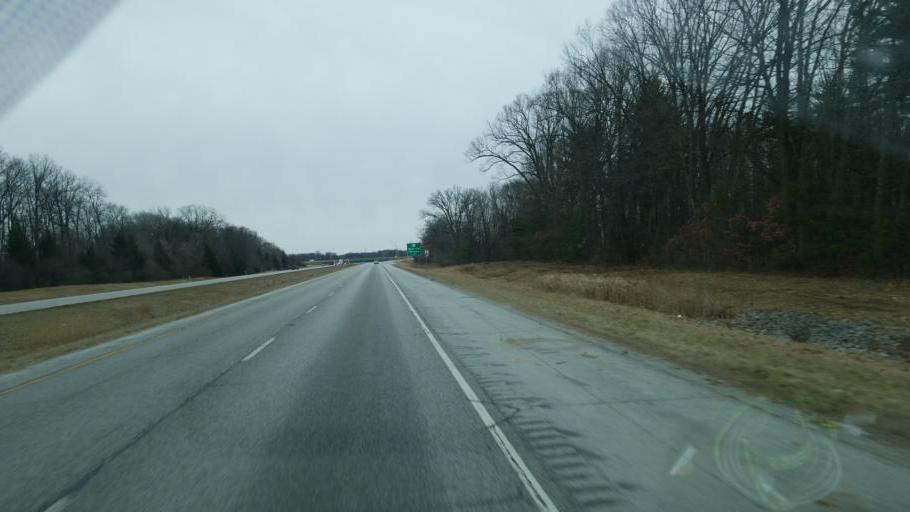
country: US
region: Indiana
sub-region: Porter County
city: Chesterton
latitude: 41.5588
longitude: -87.0467
